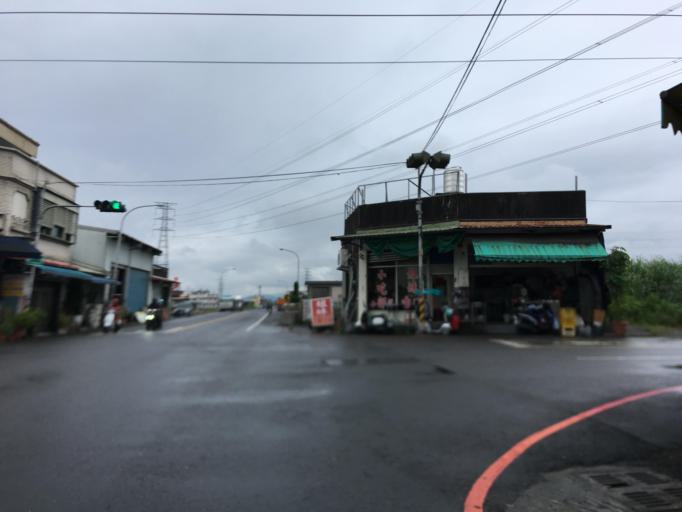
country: TW
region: Taiwan
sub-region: Yilan
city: Yilan
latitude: 24.6639
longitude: 121.7505
